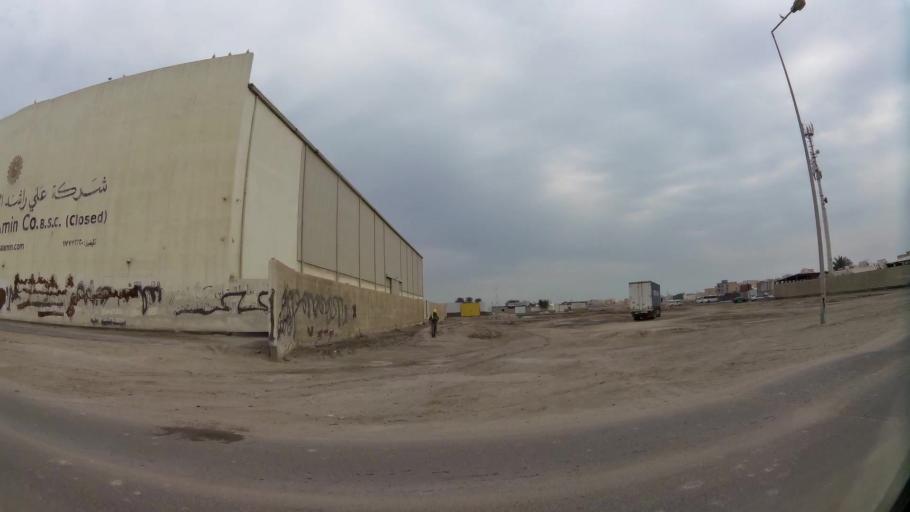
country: BH
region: Northern
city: Sitrah
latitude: 26.1719
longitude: 50.6114
